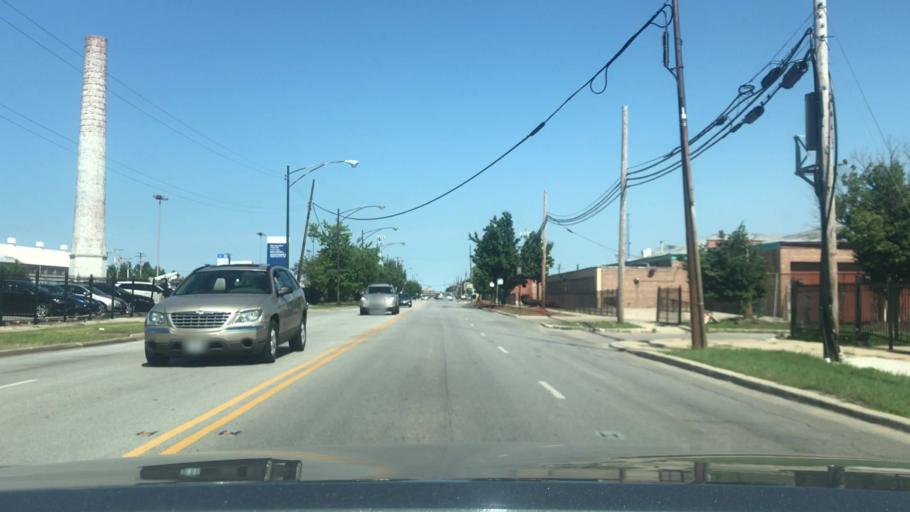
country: US
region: Illinois
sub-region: Cook County
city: Dolton
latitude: 41.7075
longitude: -87.6017
